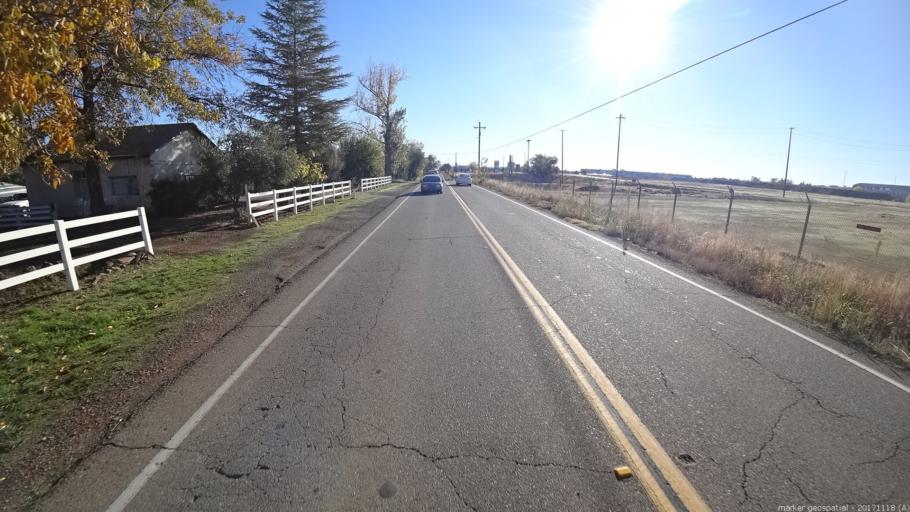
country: US
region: California
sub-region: Shasta County
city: Anderson
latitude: 40.4406
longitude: -122.2766
